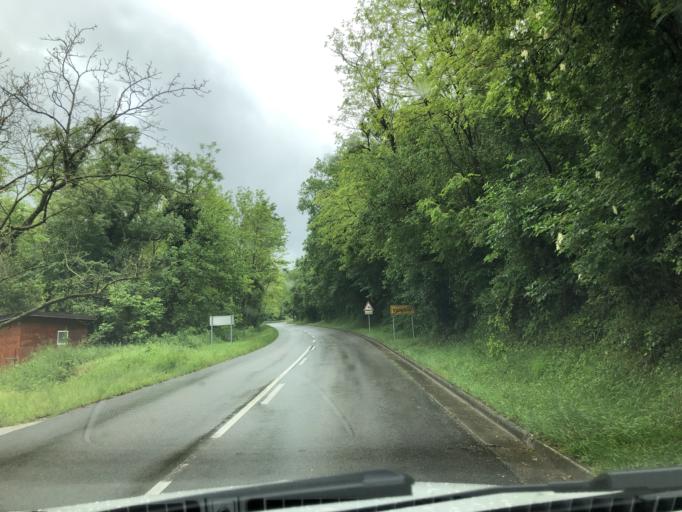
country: SI
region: Koper-Capodistria
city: Prade
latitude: 45.5158
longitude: 13.7800
